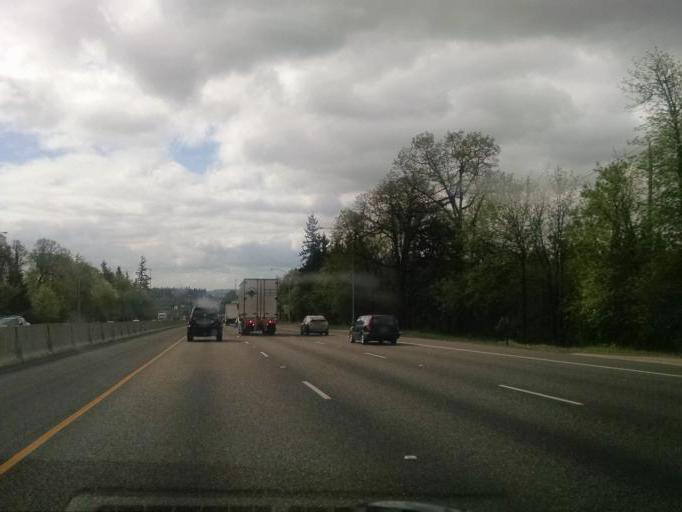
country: US
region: Oregon
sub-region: Washington County
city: Metzger
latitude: 45.4292
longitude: -122.7442
